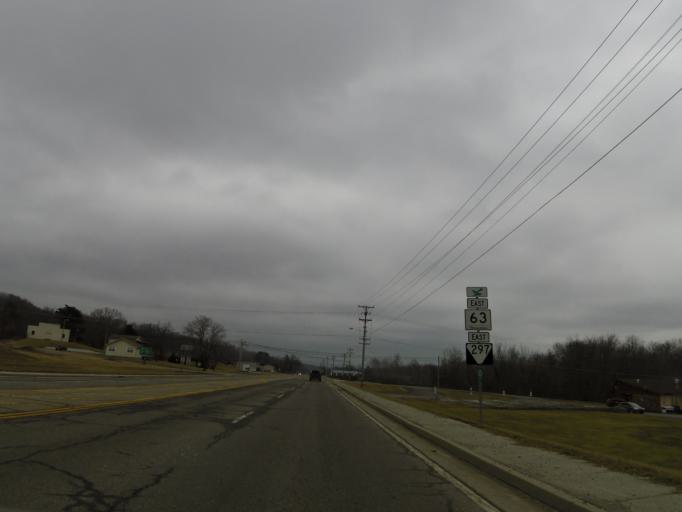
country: US
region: Tennessee
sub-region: Scott County
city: Huntsville
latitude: 36.4125
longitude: -84.5373
